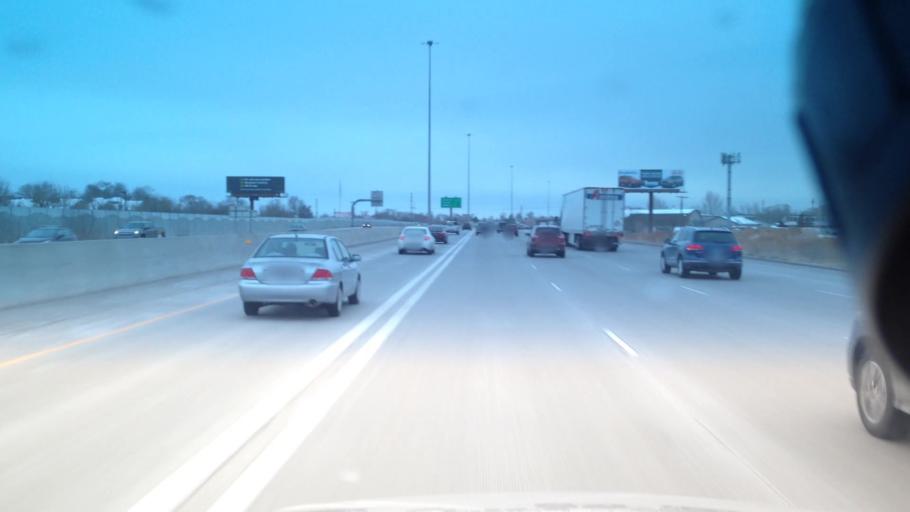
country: US
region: Utah
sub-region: Salt Lake County
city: Salt Lake City
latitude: 40.7871
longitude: -111.9135
